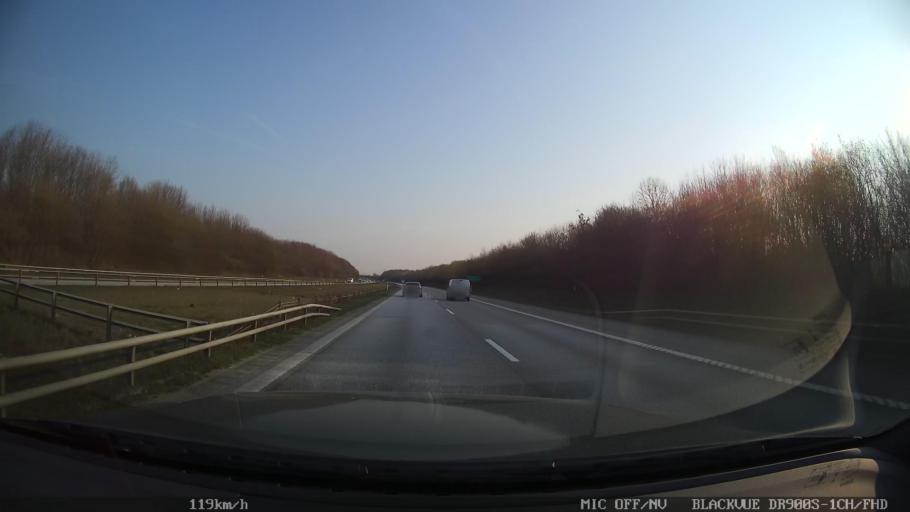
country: SE
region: Skane
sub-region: Malmo
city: Oxie
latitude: 55.5777
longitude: 13.1086
